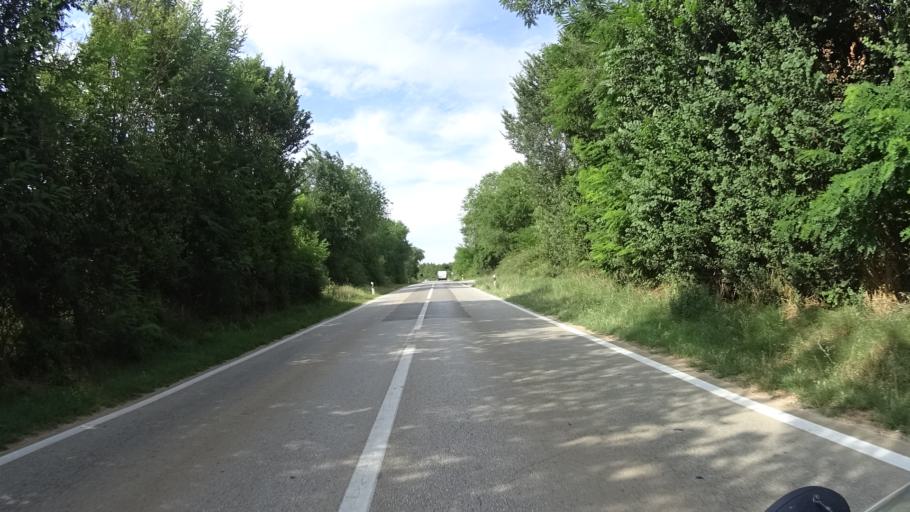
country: HR
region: Istarska
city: Galizana
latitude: 44.9070
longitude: 13.9059
